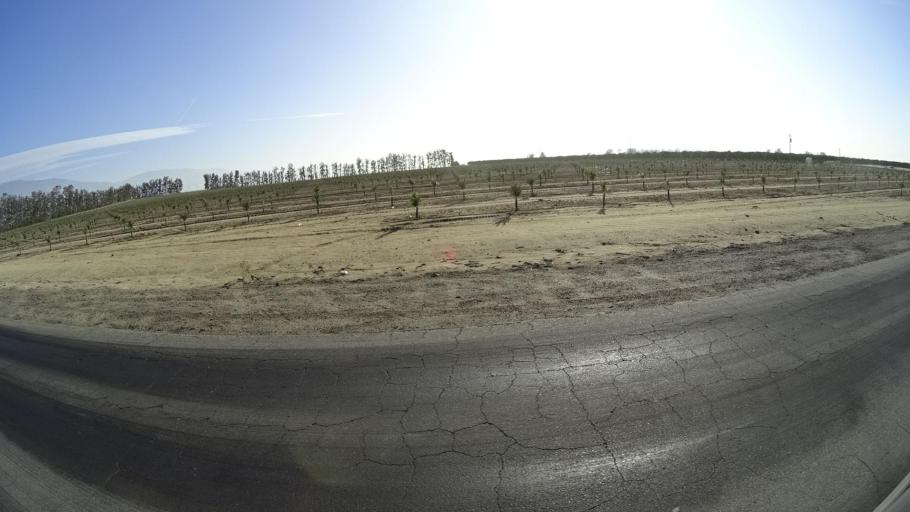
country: US
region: California
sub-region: Kern County
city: Arvin
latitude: 35.3259
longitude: -118.7792
